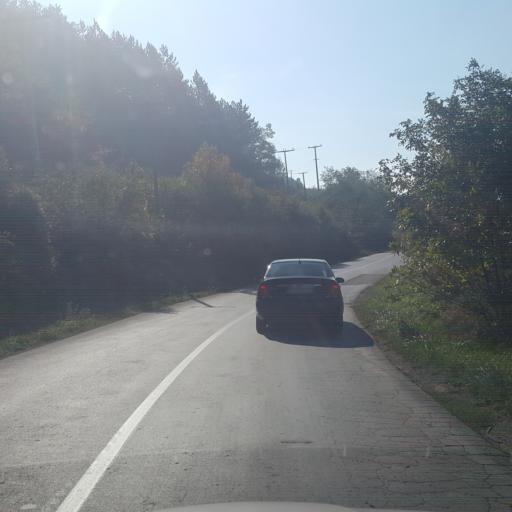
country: RS
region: Central Serbia
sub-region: Pirotski Okrug
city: Pirot
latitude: 43.1963
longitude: 22.5629
